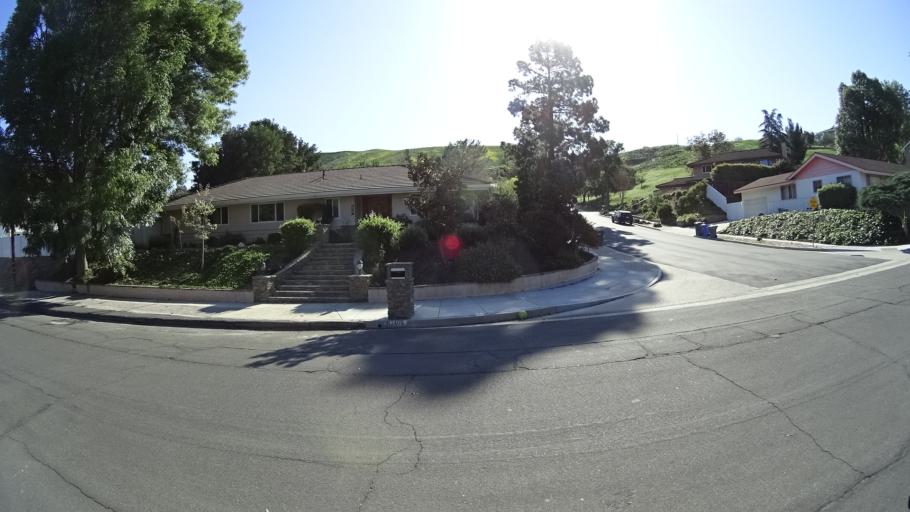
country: US
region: California
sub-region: Ventura County
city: Thousand Oaks
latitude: 34.1882
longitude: -118.8376
